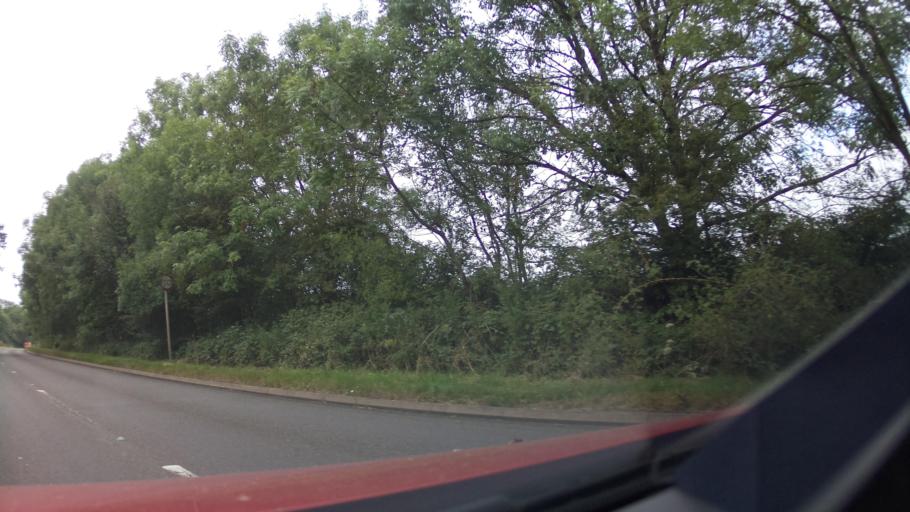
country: GB
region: England
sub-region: Staffordshire
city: Mayfield
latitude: 53.0162
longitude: -1.7802
